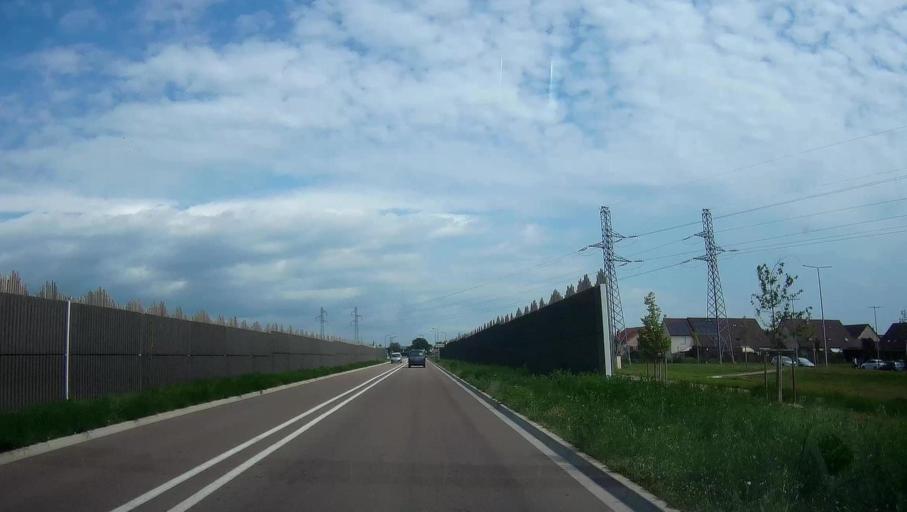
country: FR
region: Bourgogne
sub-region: Departement de la Cote-d'Or
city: Beaune
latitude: 47.0250
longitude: 4.8585
